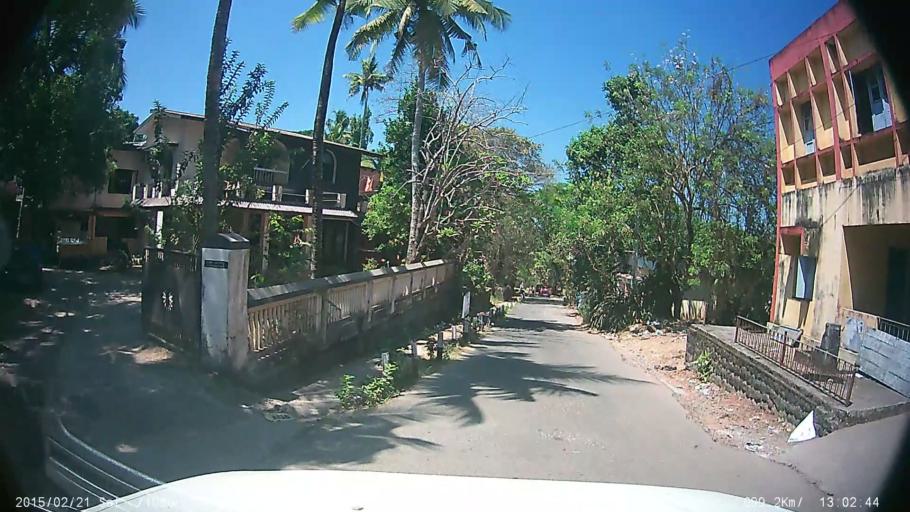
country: IN
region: Kerala
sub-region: Kottayam
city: Kottayam
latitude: 9.5913
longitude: 76.5357
